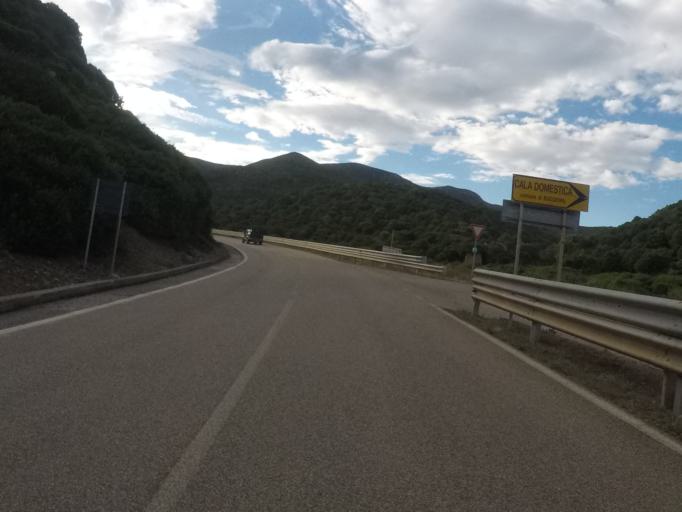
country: IT
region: Sardinia
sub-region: Provincia di Carbonia-Iglesias
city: Buggerru
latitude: 39.3684
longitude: 8.3948
